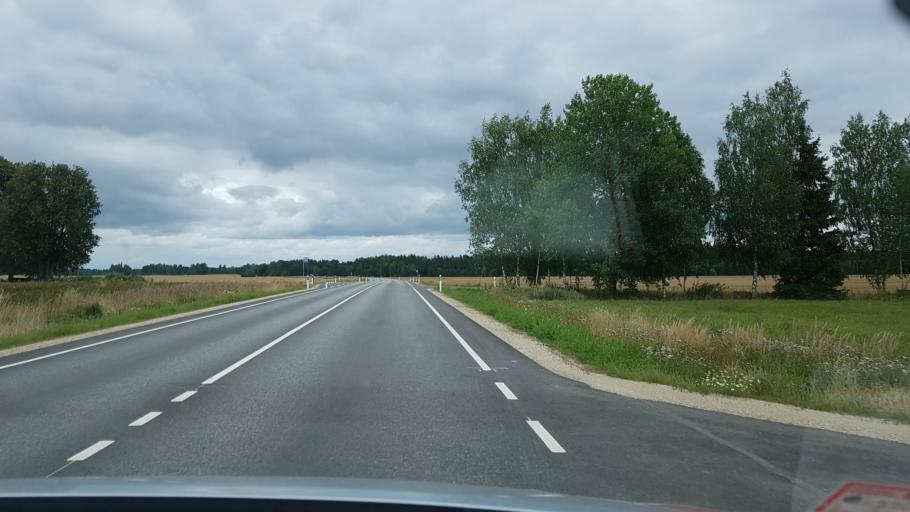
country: EE
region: Polvamaa
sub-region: Raepina vald
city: Rapina
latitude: 58.0813
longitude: 27.3070
